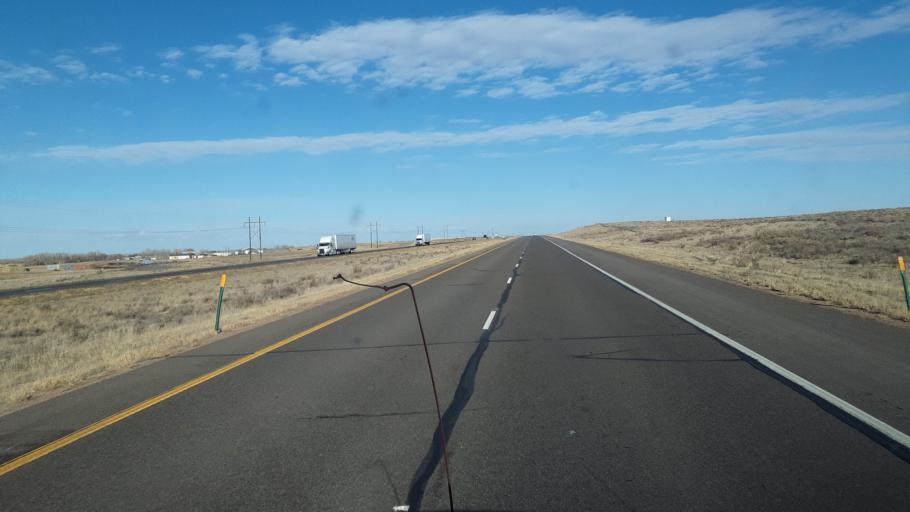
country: US
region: Colorado
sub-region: Morgan County
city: Brush
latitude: 40.3137
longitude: -103.5060
